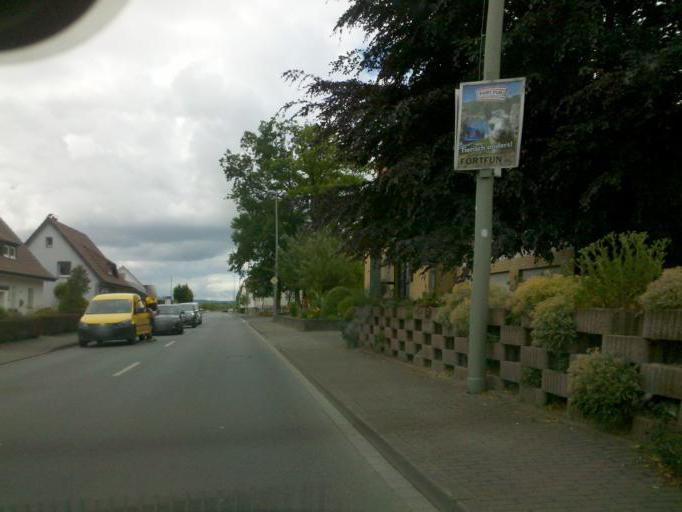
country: DE
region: North Rhine-Westphalia
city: Erwitte
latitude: 51.6197
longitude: 8.3075
